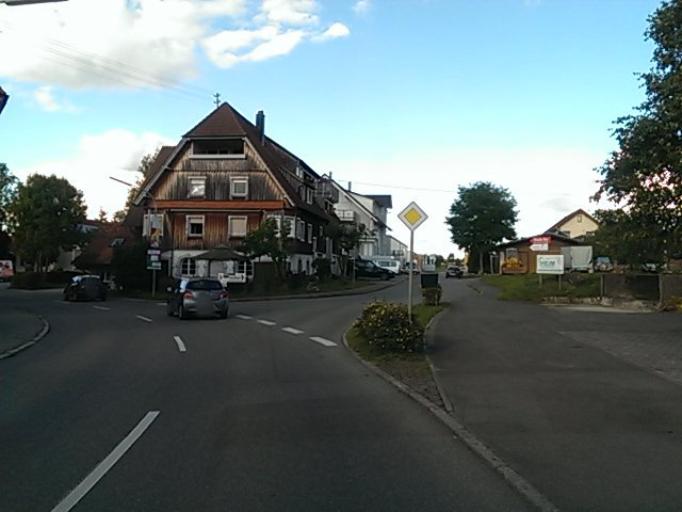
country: DE
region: Baden-Wuerttemberg
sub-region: Freiburg Region
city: Seedorf
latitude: 48.2888
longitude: 8.4944
